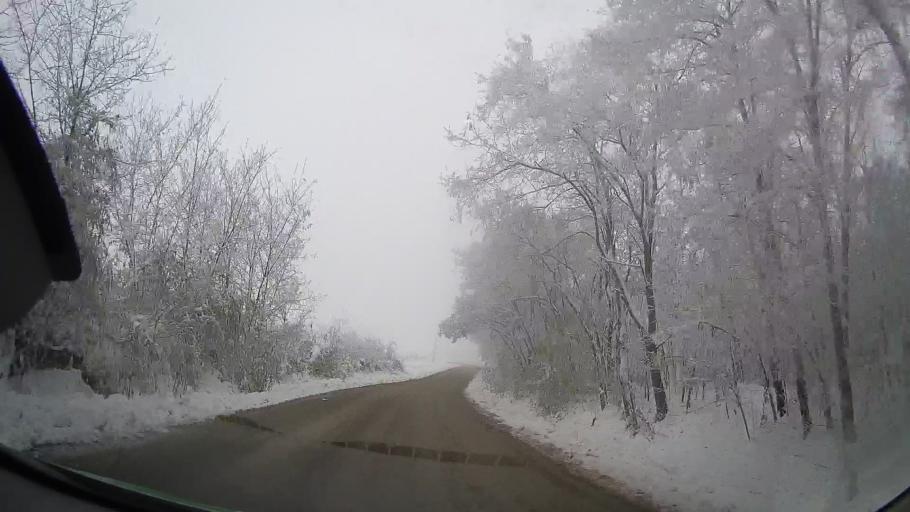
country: RO
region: Iasi
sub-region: Comuna Tansa
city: Suhulet
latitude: 46.8968
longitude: 27.2450
